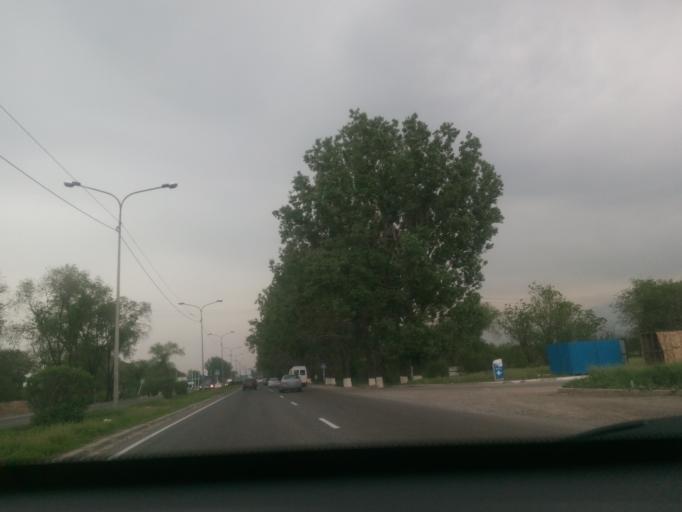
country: KZ
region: Almaty Oblysy
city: Burunday
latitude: 43.2280
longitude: 76.7533
